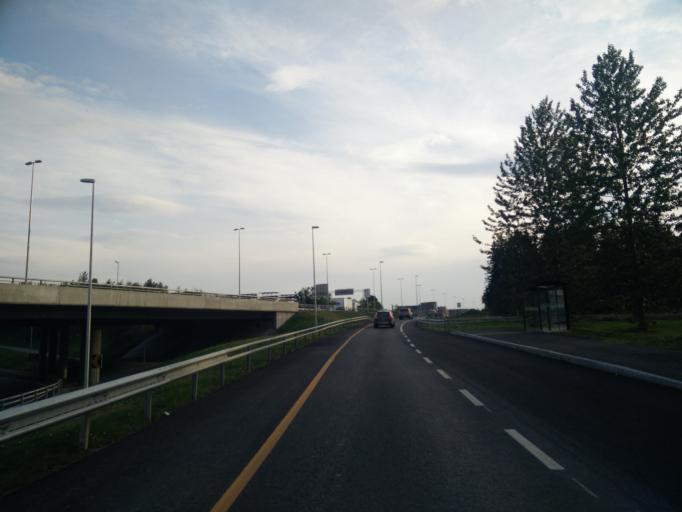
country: NO
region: Sor-Trondelag
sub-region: Trondheim
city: Trondheim
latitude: 63.4262
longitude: 10.4758
